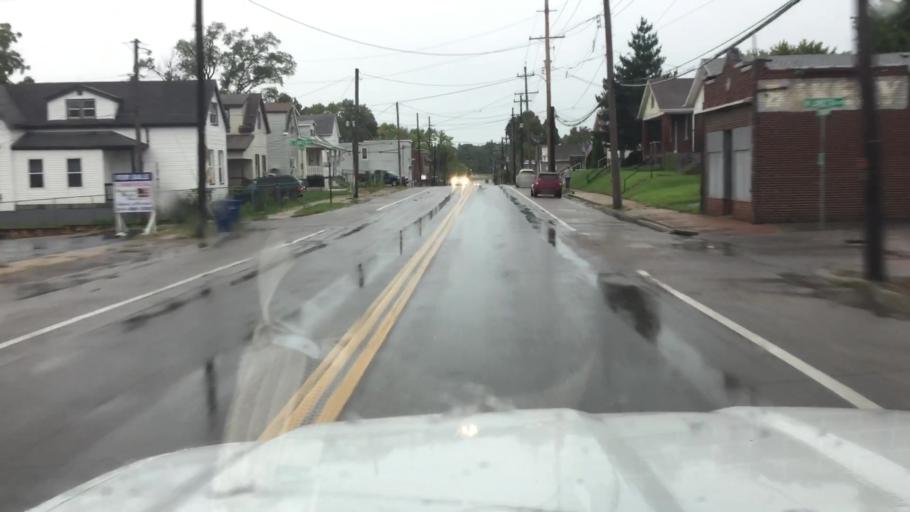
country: US
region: Missouri
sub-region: Saint Louis County
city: Lemay
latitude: 38.5284
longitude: -90.2772
